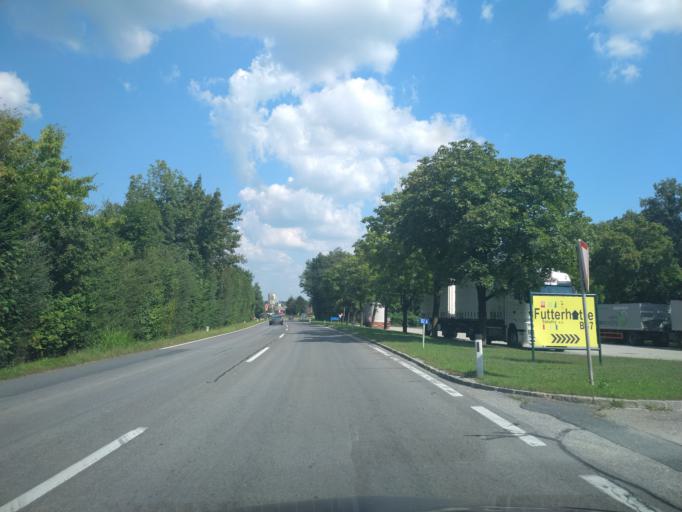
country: AT
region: Styria
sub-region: Politischer Bezirk Leibnitz
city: Gabersdorf
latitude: 46.7658
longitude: 15.5739
